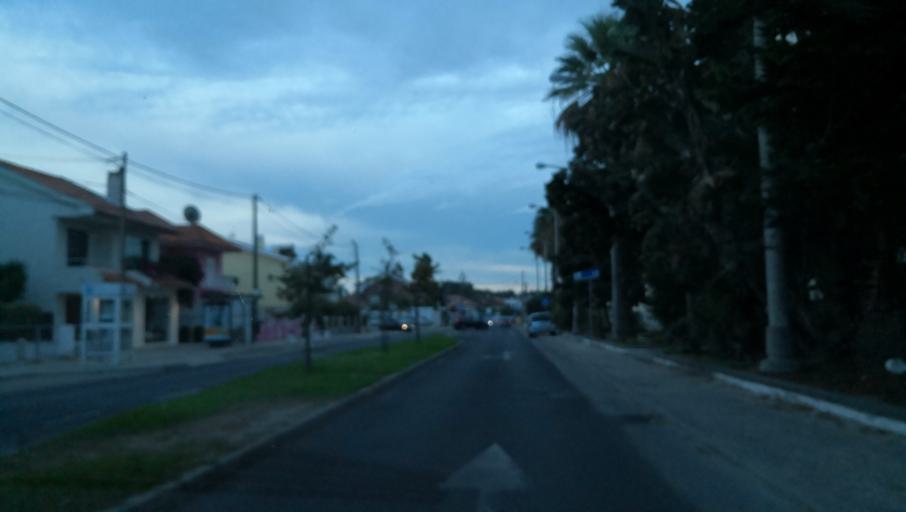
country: PT
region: Setubal
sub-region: Almada
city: Charneca
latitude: 38.6091
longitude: -9.1879
